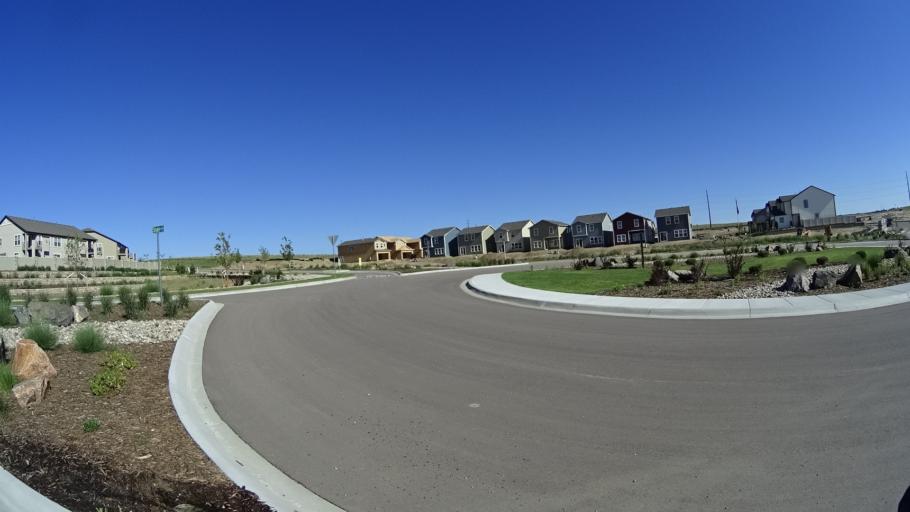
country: US
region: Colorado
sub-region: El Paso County
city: Cimarron Hills
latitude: 38.8965
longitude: -104.6767
